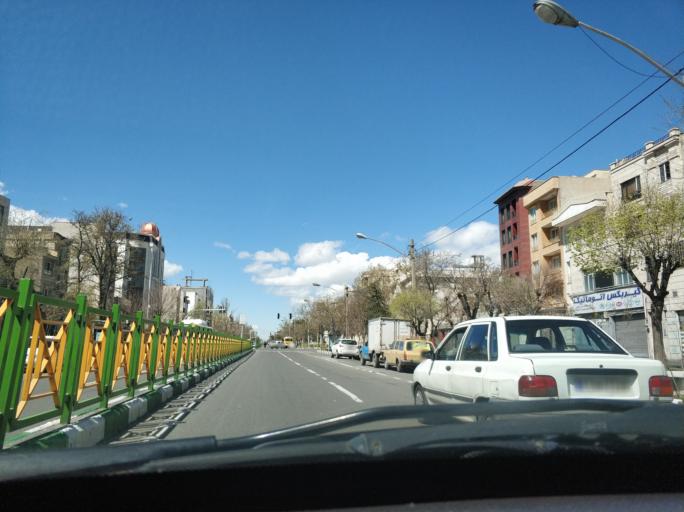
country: IR
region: Tehran
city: Tehran
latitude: 35.7199
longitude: 51.4972
